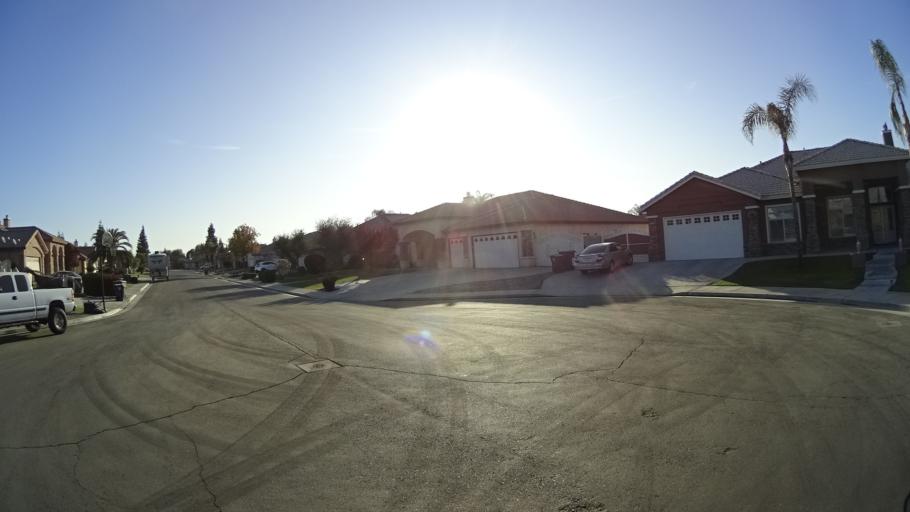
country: US
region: California
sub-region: Kern County
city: Greenfield
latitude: 35.2719
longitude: -119.0543
